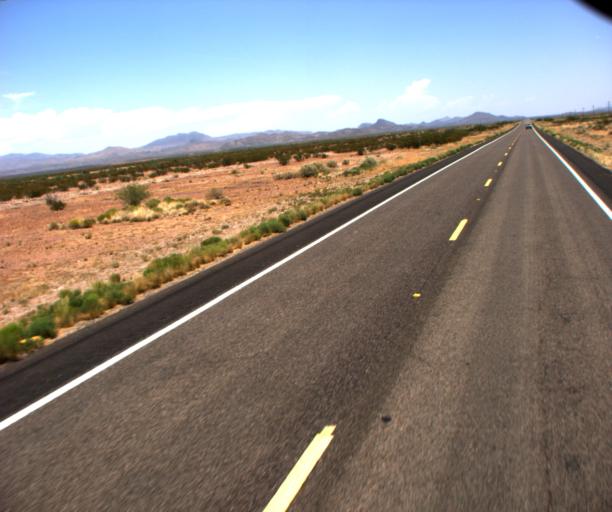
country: US
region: Arizona
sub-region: Graham County
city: Safford
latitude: 32.7789
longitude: -109.5202
